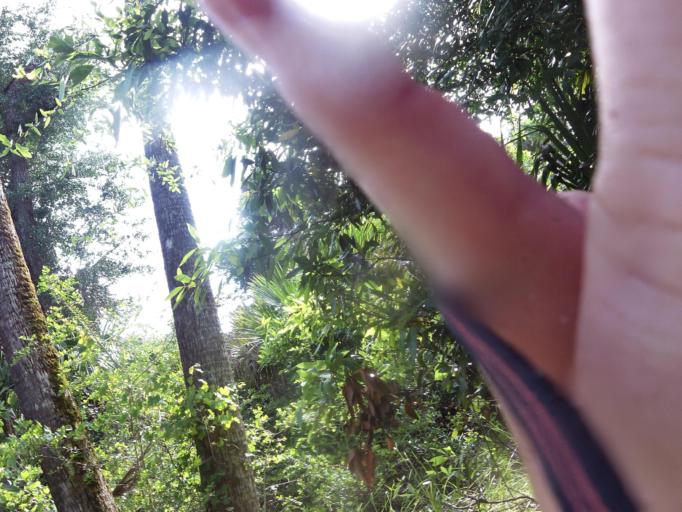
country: US
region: Florida
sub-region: Flagler County
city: Palm Coast
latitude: 29.6387
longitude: -81.2091
